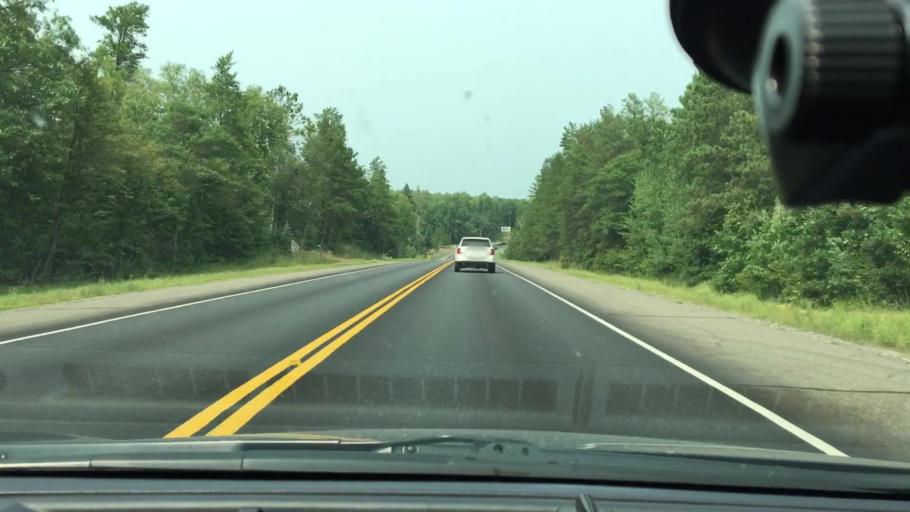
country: US
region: Minnesota
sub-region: Crow Wing County
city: Cross Lake
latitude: 46.6235
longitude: -94.1318
